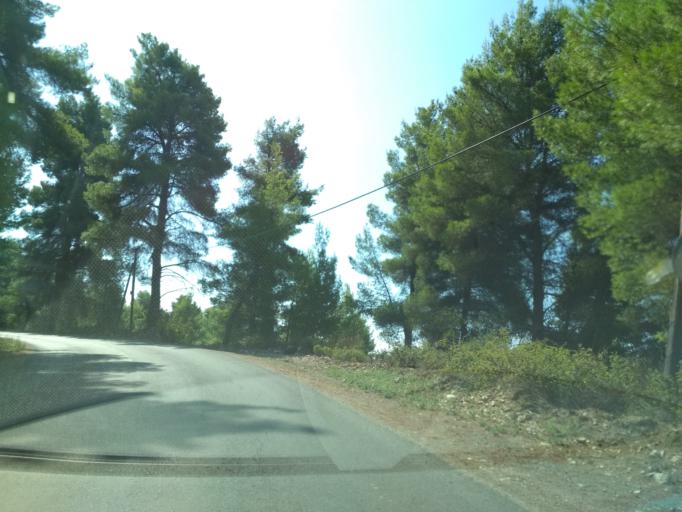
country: GR
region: Central Greece
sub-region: Nomos Evvoias
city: Roviai
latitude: 38.8160
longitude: 23.2739
